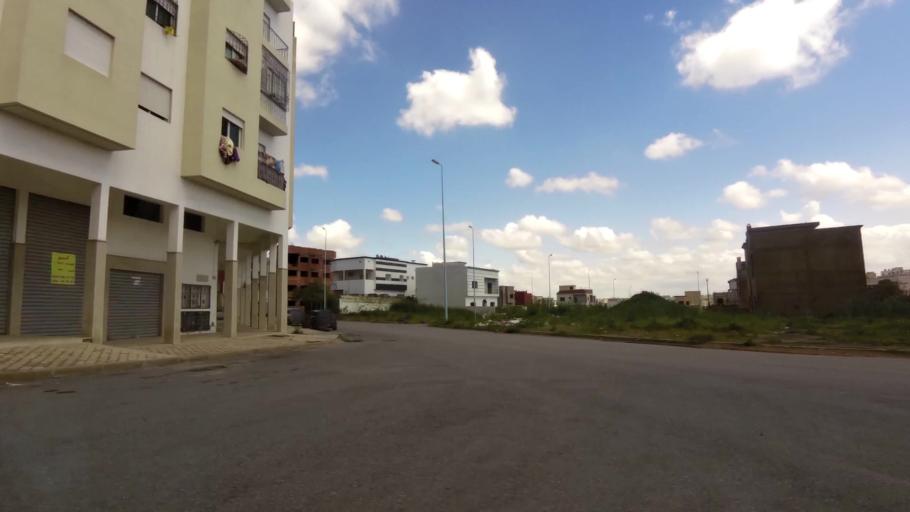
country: MA
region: Grand Casablanca
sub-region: Nouaceur
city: Dar Bouazza
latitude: 33.4228
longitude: -7.8476
